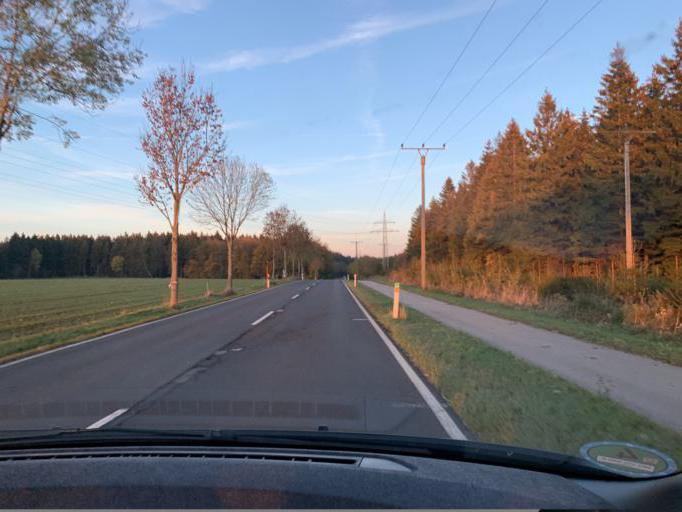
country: DE
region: North Rhine-Westphalia
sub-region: Regierungsbezirk Koln
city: Hurtgenwald
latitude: 50.6475
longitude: 6.3542
